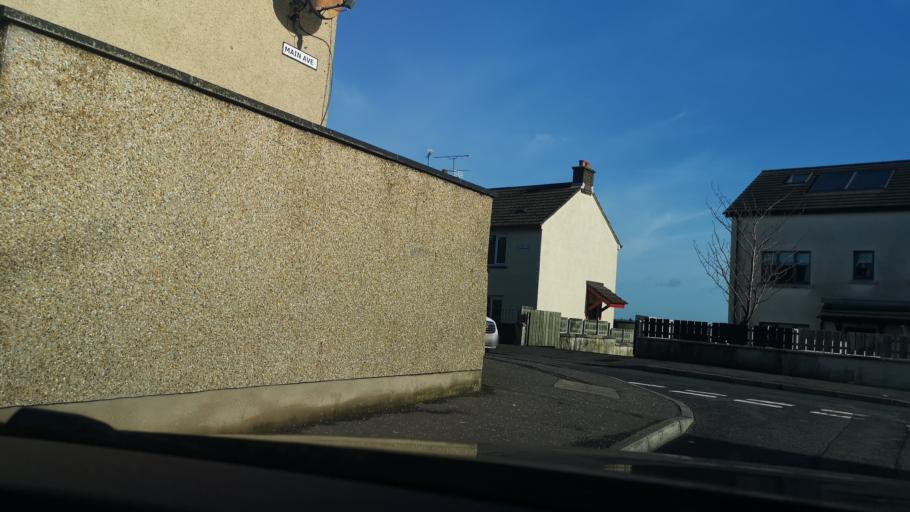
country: GB
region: Northern Ireland
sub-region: Newry and Mourne District
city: Newry
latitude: 54.1858
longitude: -6.3547
